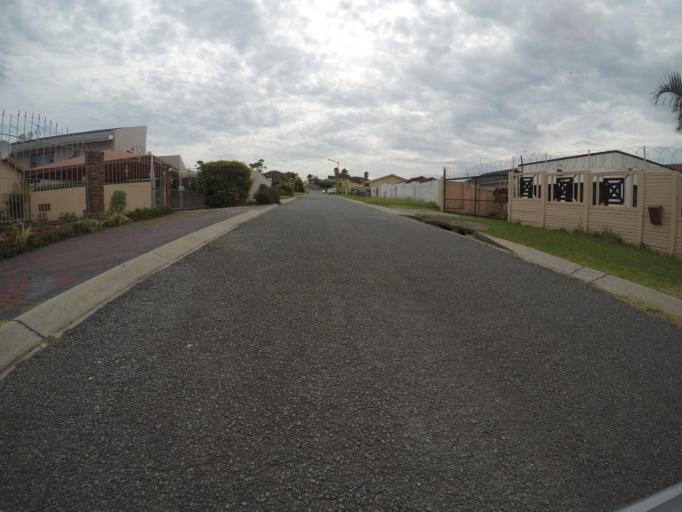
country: ZA
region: Eastern Cape
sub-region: Buffalo City Metropolitan Municipality
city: East London
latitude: -33.0007
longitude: 27.8827
